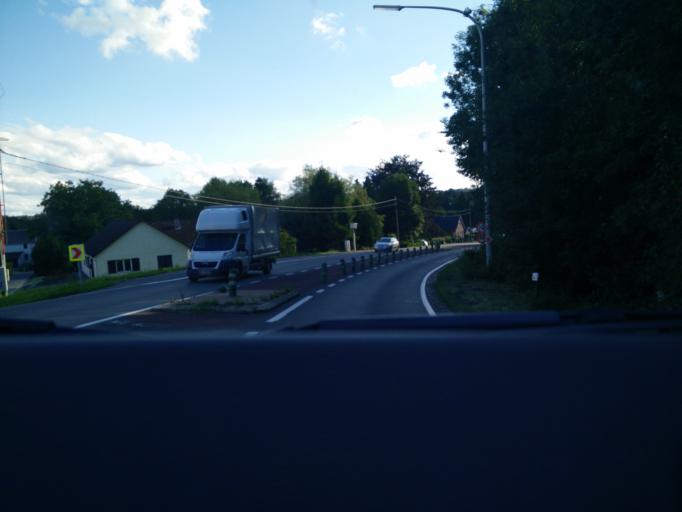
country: BE
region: Wallonia
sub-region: Province du Hainaut
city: Beaumont
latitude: 50.2318
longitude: 4.2371
